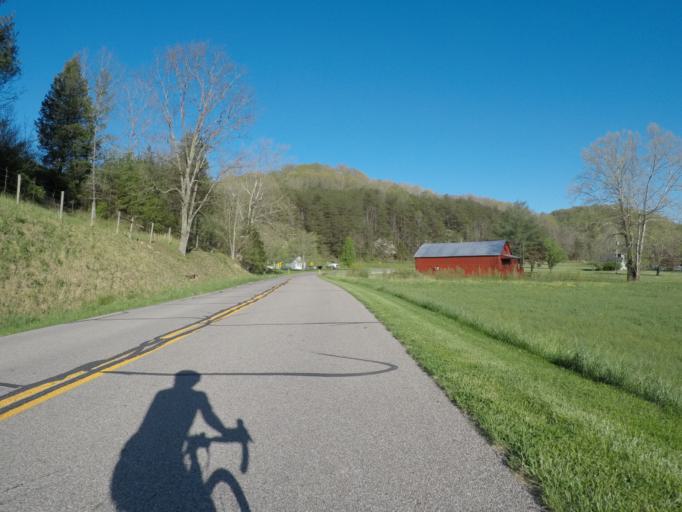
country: US
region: Kentucky
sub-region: Boyd County
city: Meads
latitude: 38.3661
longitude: -82.6798
